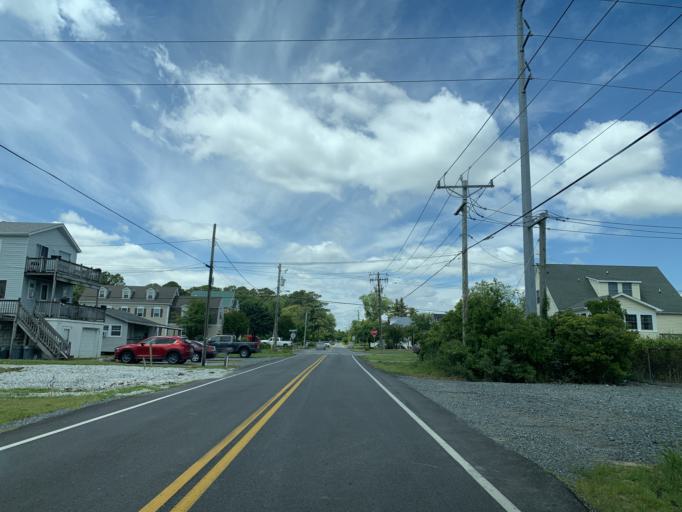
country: US
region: Maryland
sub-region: Worcester County
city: West Ocean City
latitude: 38.3314
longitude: -75.1057
